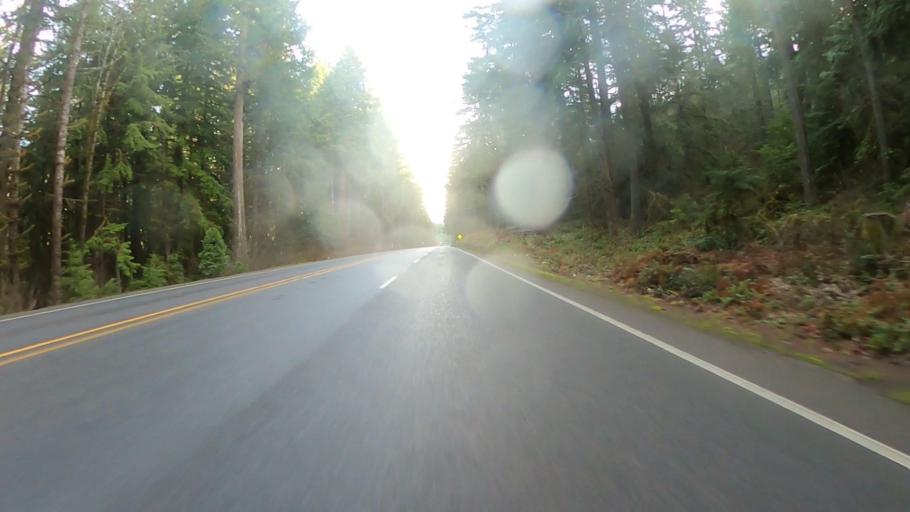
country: US
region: Oregon
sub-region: Lane County
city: Oakridge
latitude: 43.7311
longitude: -122.4032
